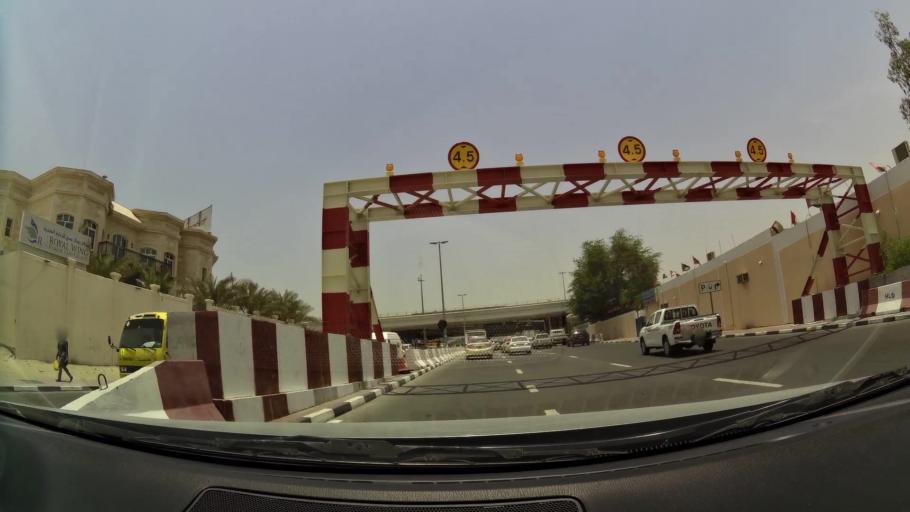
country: AE
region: Ash Shariqah
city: Sharjah
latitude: 25.2305
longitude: 55.3886
